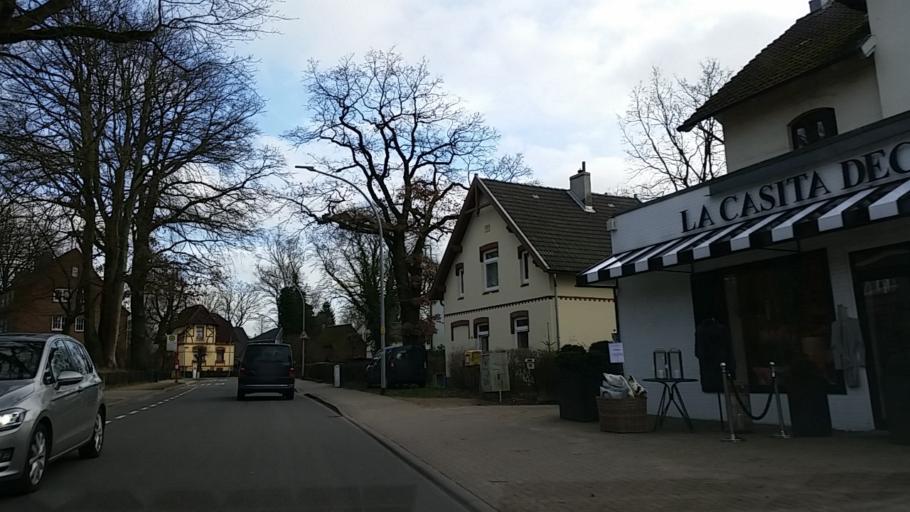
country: DE
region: Schleswig-Holstein
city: Wentorf bei Hamburg
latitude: 53.5018
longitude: 10.2507
